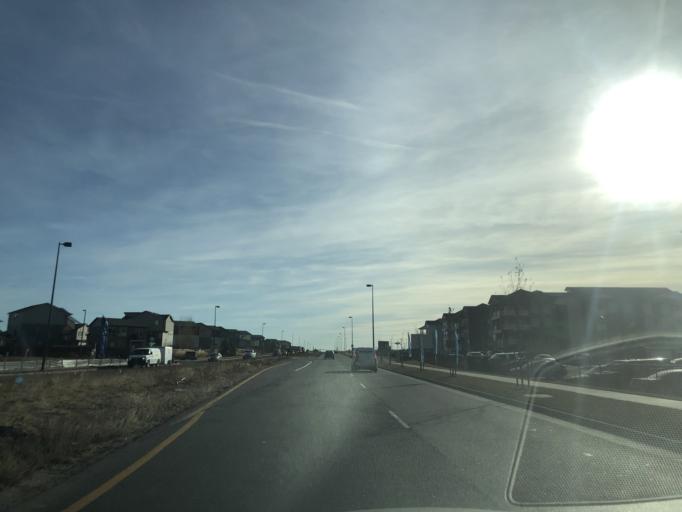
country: US
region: Colorado
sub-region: Adams County
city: Aurora
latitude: 39.7936
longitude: -104.7721
